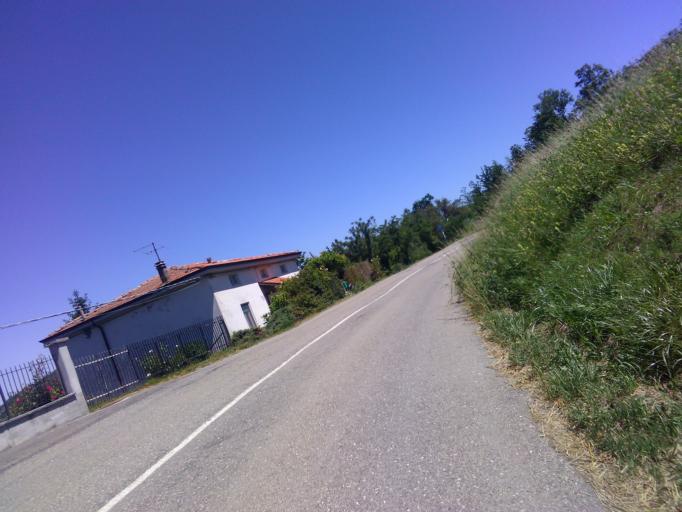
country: IT
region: Emilia-Romagna
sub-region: Provincia di Parma
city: Berceto
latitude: 44.5596
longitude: 10.0370
